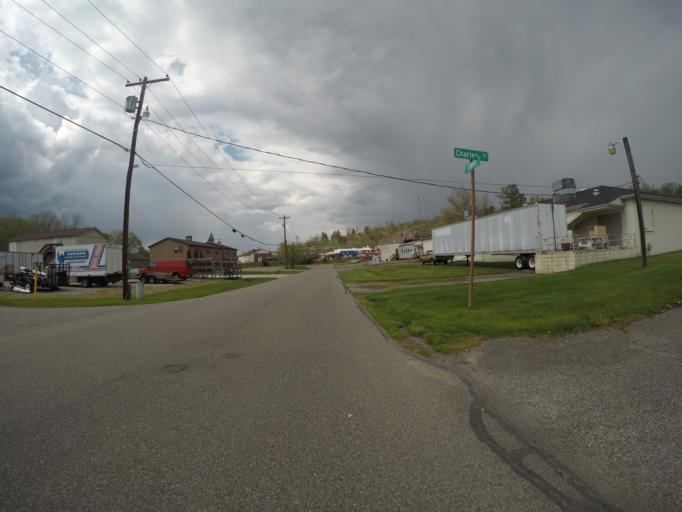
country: US
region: Ohio
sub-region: Washington County
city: Marietta
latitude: 39.4135
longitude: -81.4401
